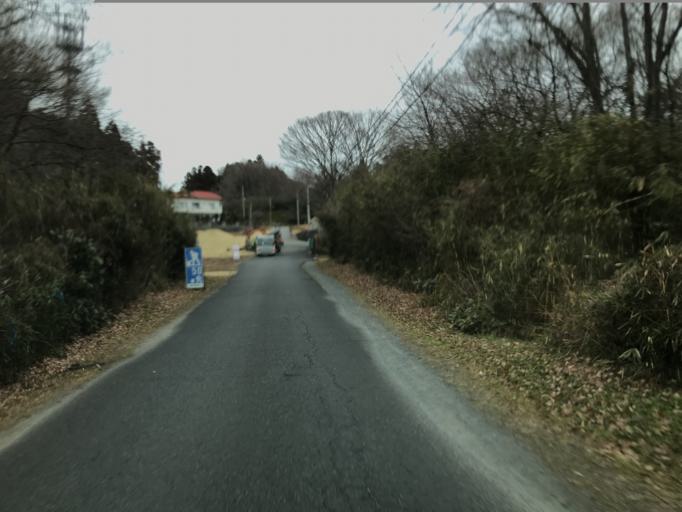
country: JP
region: Fukushima
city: Iwaki
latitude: 37.0634
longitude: 140.9070
